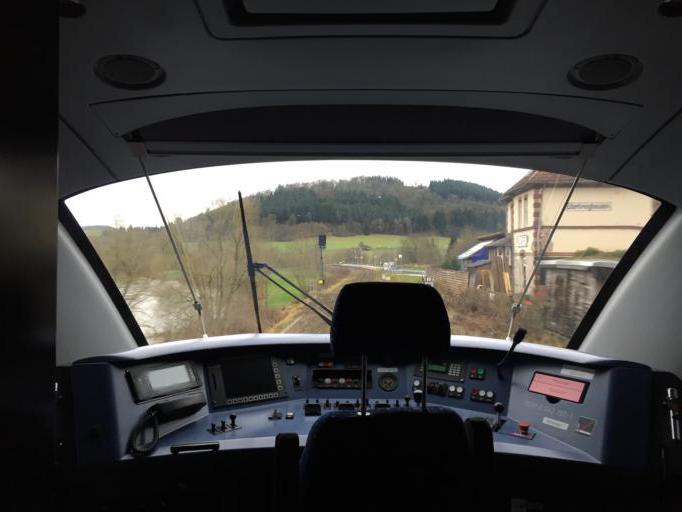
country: DE
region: Hesse
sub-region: Regierungsbezirk Kassel
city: Frankenau
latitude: 51.1305
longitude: 8.8729
